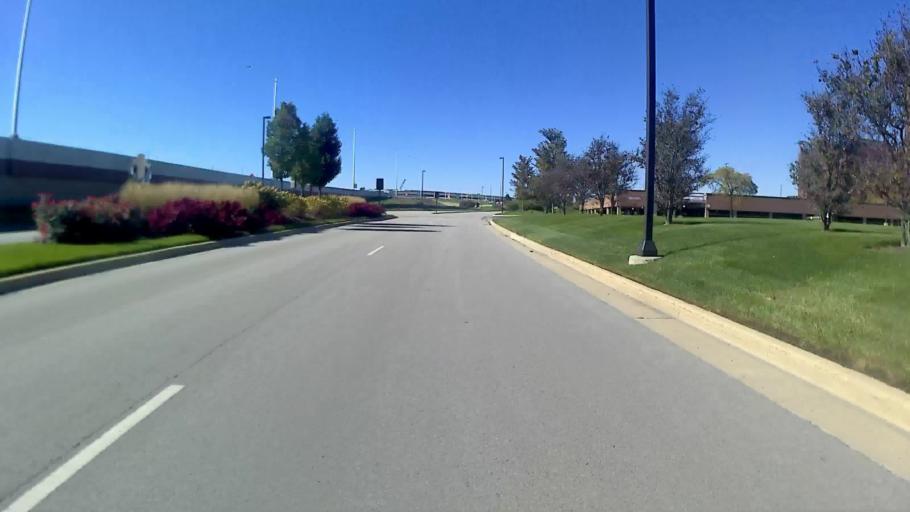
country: US
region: Illinois
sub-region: DuPage County
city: Itasca
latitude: 41.9846
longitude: -88.0167
